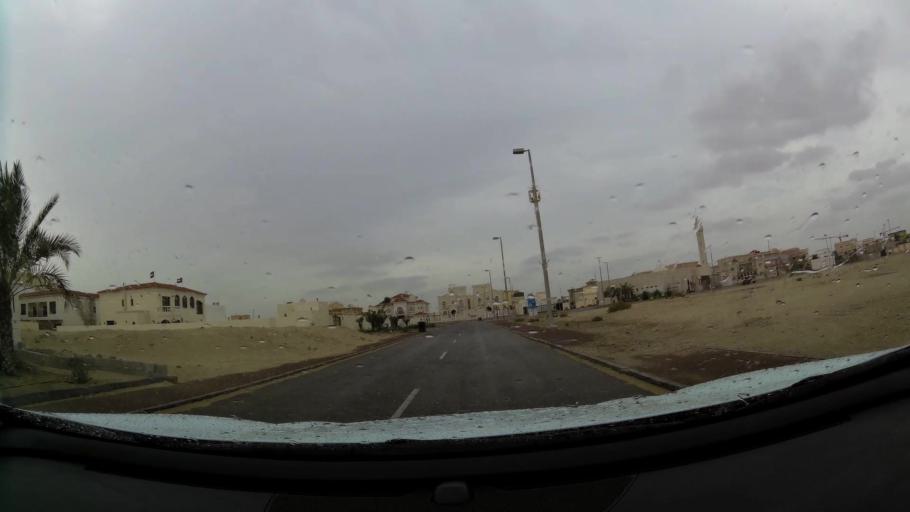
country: AE
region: Abu Dhabi
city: Abu Dhabi
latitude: 24.3654
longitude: 54.6394
